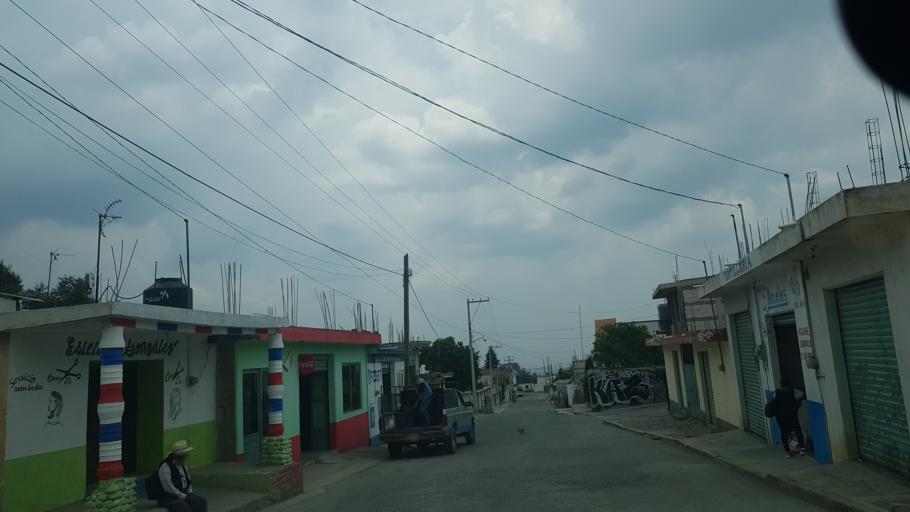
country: MX
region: Puebla
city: Domingo Arenas
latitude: 19.1523
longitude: -98.4864
